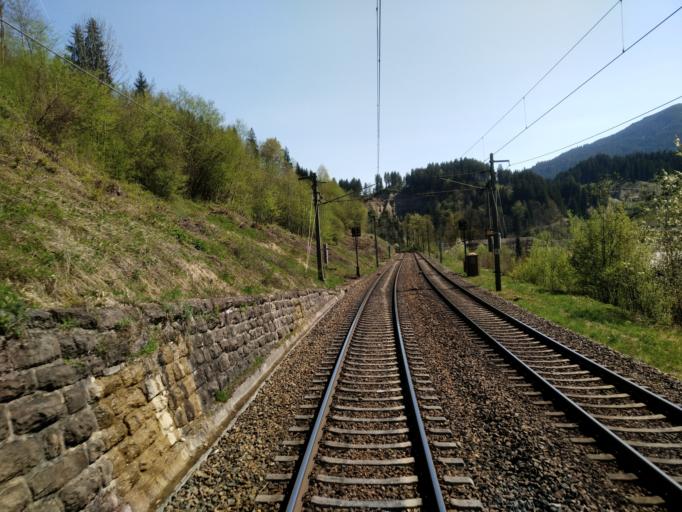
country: AT
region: Tyrol
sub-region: Politischer Bezirk Kitzbuhel
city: Hopfgarten im Brixental
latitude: 47.4422
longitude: 12.1646
